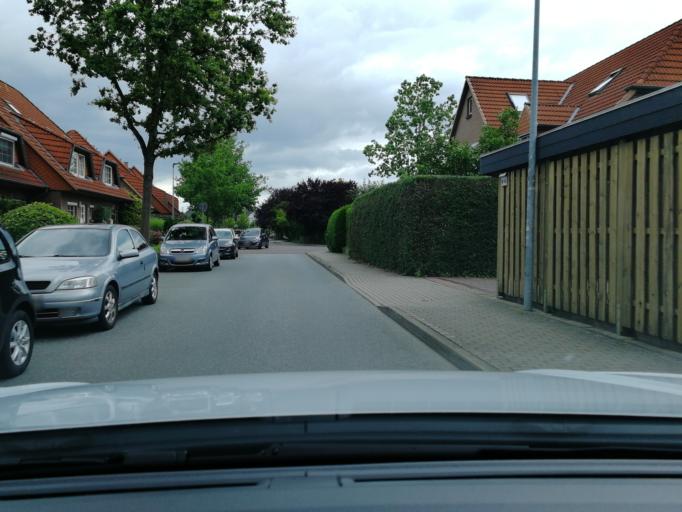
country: DE
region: Schleswig-Holstein
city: Schwarzenbek
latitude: 53.5112
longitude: 10.4838
